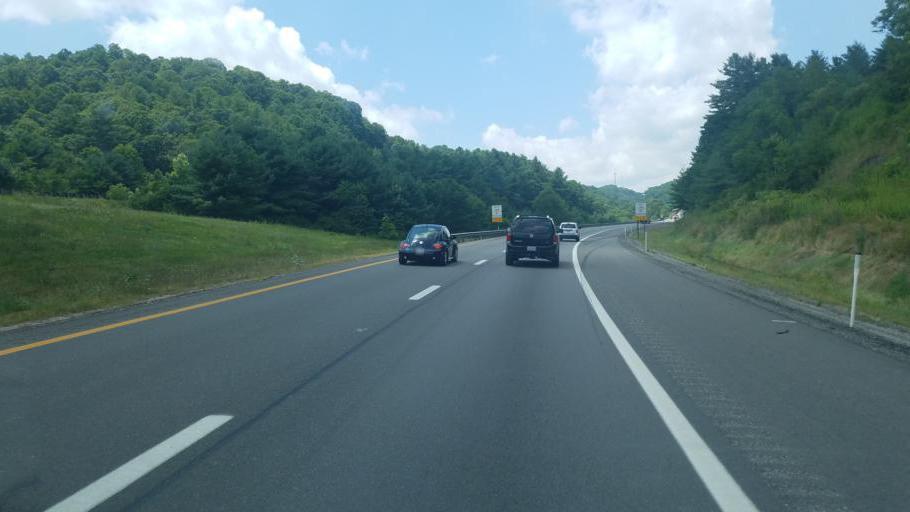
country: US
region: West Virginia
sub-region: Raleigh County
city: Beaver
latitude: 37.7183
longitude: -81.1618
